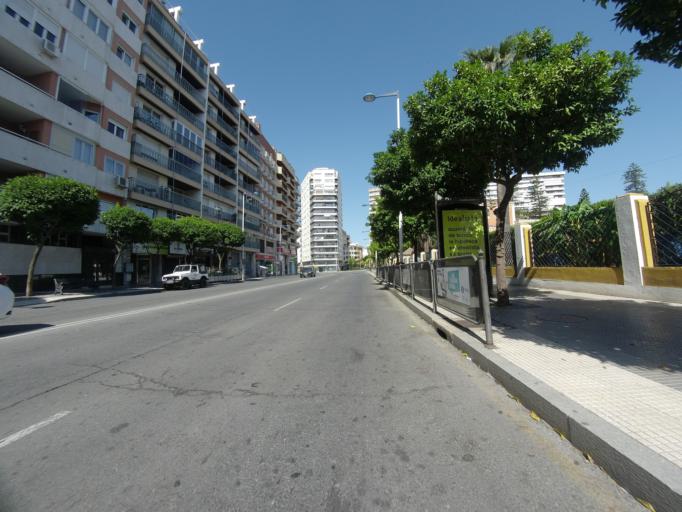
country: ES
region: Andalusia
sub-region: Provincia de Huelva
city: Huelva
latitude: 37.2546
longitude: -6.9452
